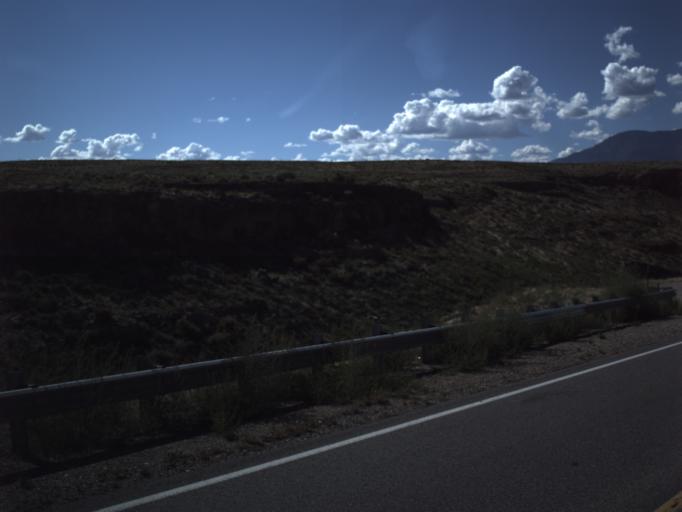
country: US
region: Utah
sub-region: Washington County
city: Hurricane
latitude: 37.1673
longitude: -113.2640
